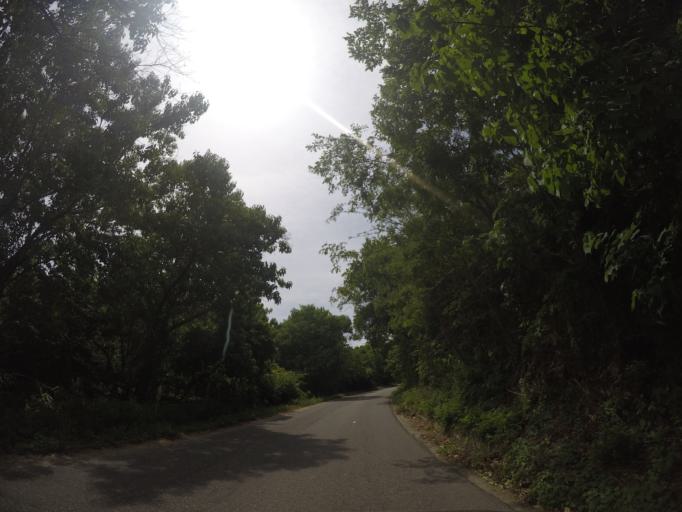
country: MX
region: Oaxaca
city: Santa Maria Tonameca
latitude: 15.6680
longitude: -96.5324
